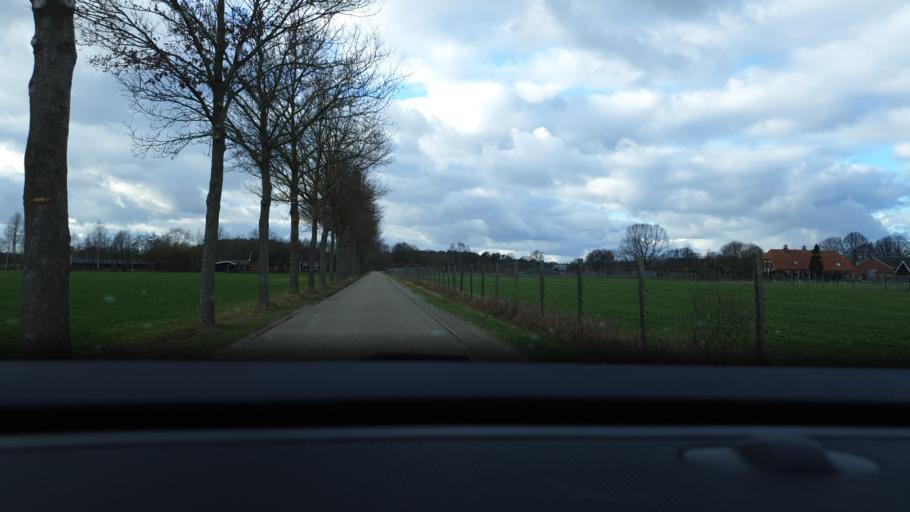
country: NL
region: Gelderland
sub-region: Oude IJsselstreek
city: Wisch
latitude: 51.9761
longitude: 6.3950
